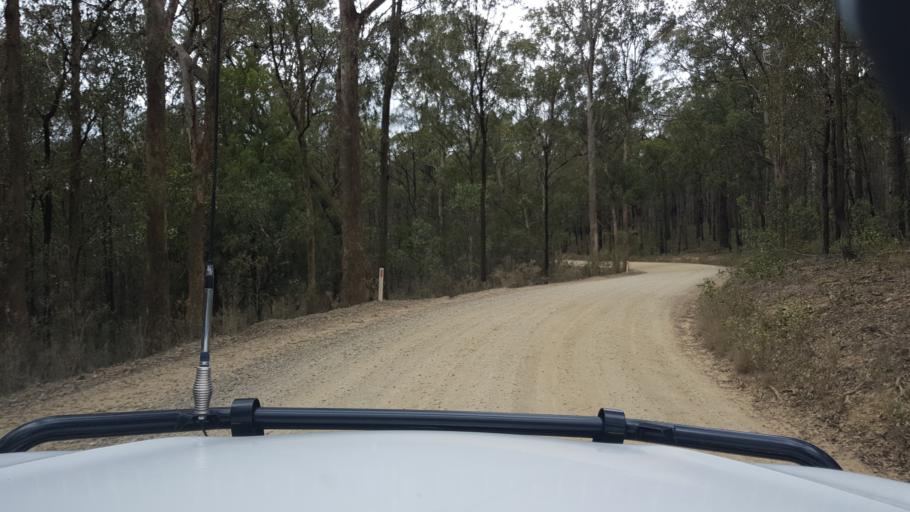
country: AU
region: Victoria
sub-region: East Gippsland
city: Bairnsdale
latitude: -37.7006
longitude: 147.5795
